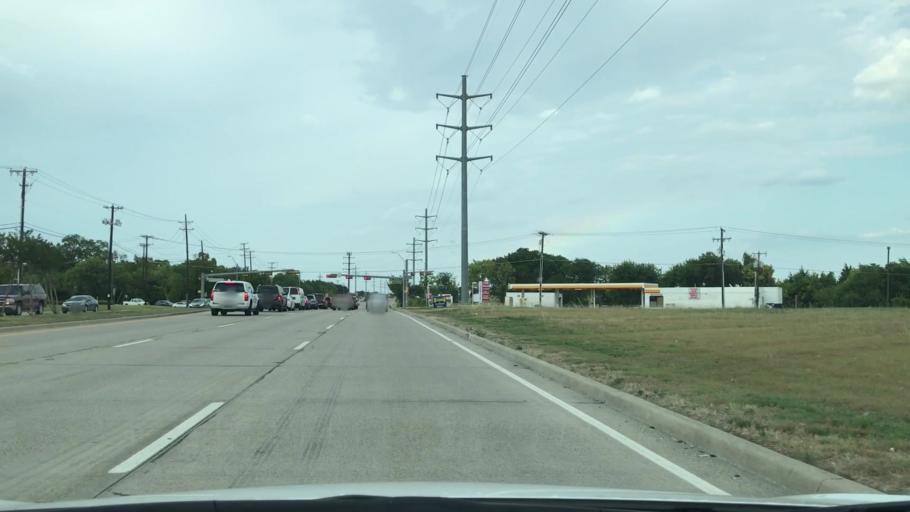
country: US
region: Texas
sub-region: Dallas County
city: Rowlett
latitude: 32.9099
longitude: -96.5327
